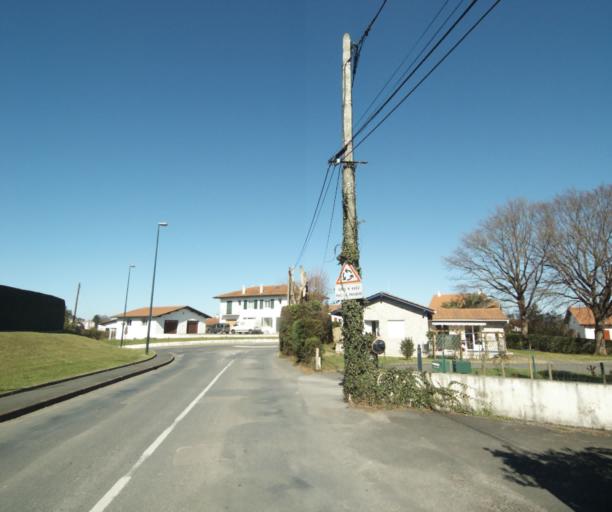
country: FR
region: Aquitaine
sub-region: Departement des Pyrenees-Atlantiques
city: Ciboure
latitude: 43.3767
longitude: -1.6691
